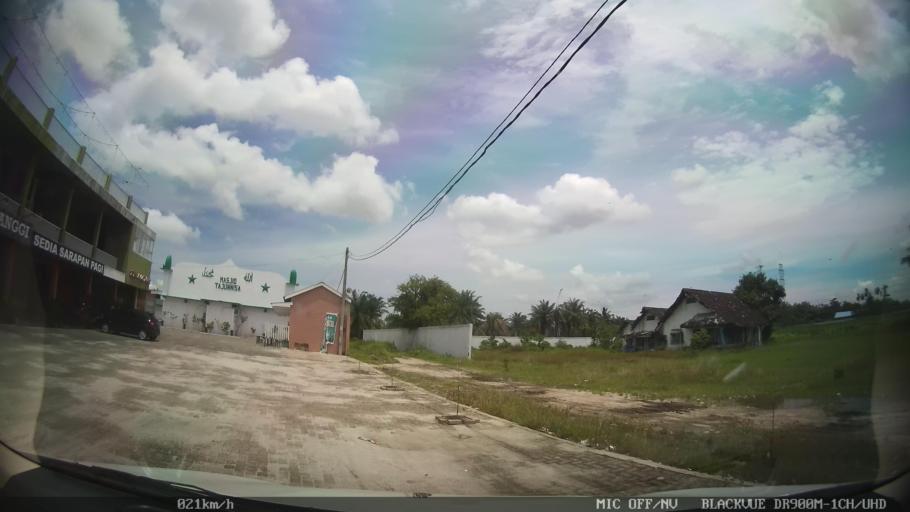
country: ID
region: North Sumatra
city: Percut
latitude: 3.5874
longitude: 98.8833
